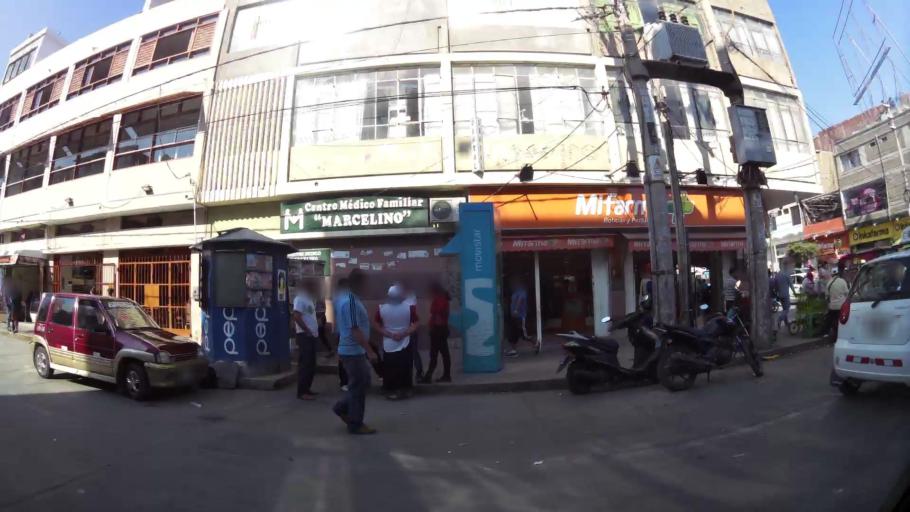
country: PE
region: Lambayeque
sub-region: Provincia de Chiclayo
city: Chiclayo
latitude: -6.7676
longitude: -79.8404
